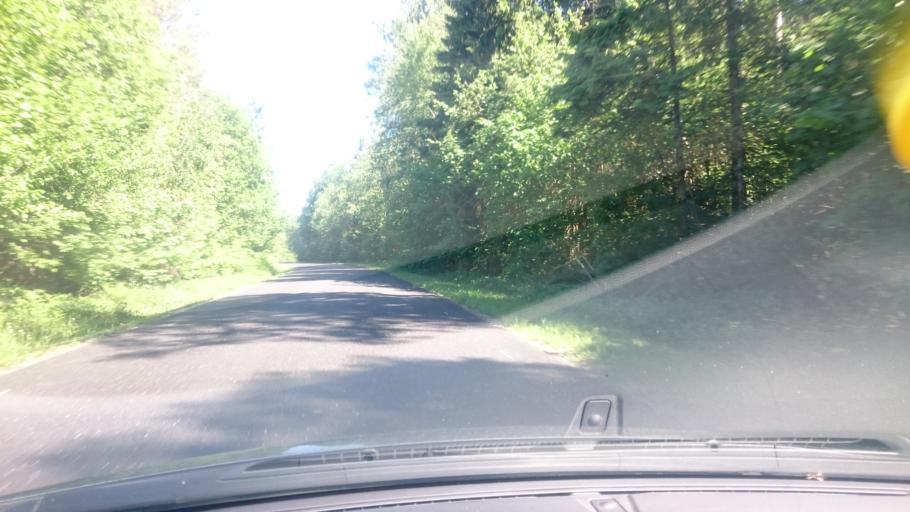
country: EE
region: Harju
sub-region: Rae vald
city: Vaida
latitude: 59.2157
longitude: 24.9544
